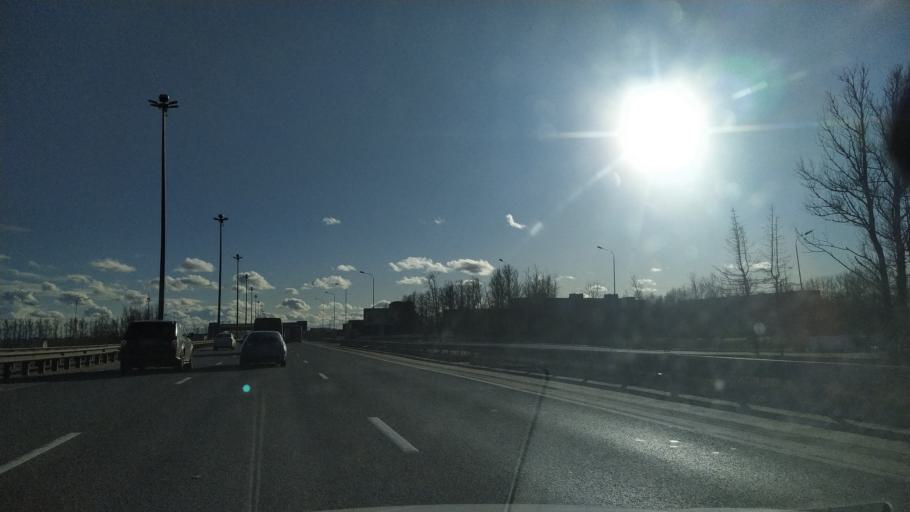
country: RU
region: St.-Petersburg
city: Aleksandrovskaya
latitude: 59.7551
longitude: 30.3207
